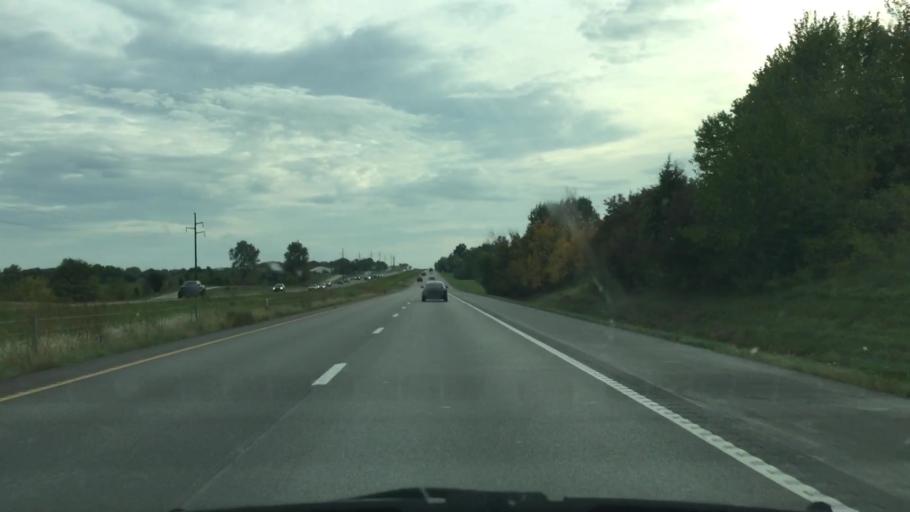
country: US
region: Missouri
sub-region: Clay County
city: Kearney
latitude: 39.3138
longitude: -94.4015
